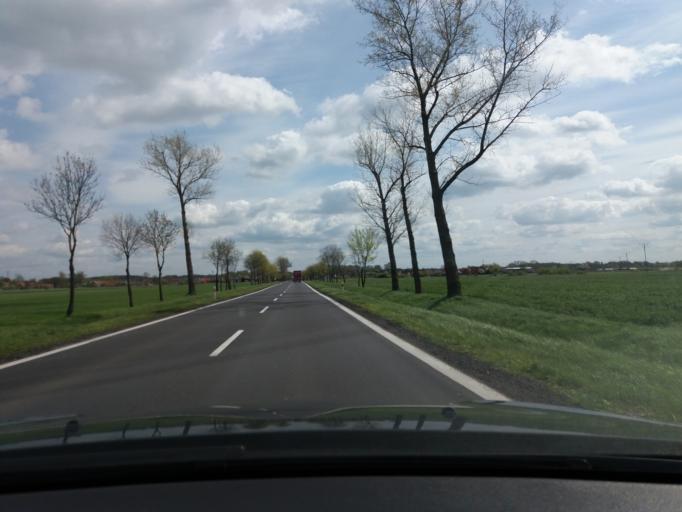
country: PL
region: Lower Silesian Voivodeship
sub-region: Powiat legnicki
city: Prochowice
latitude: 51.2386
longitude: 16.4161
